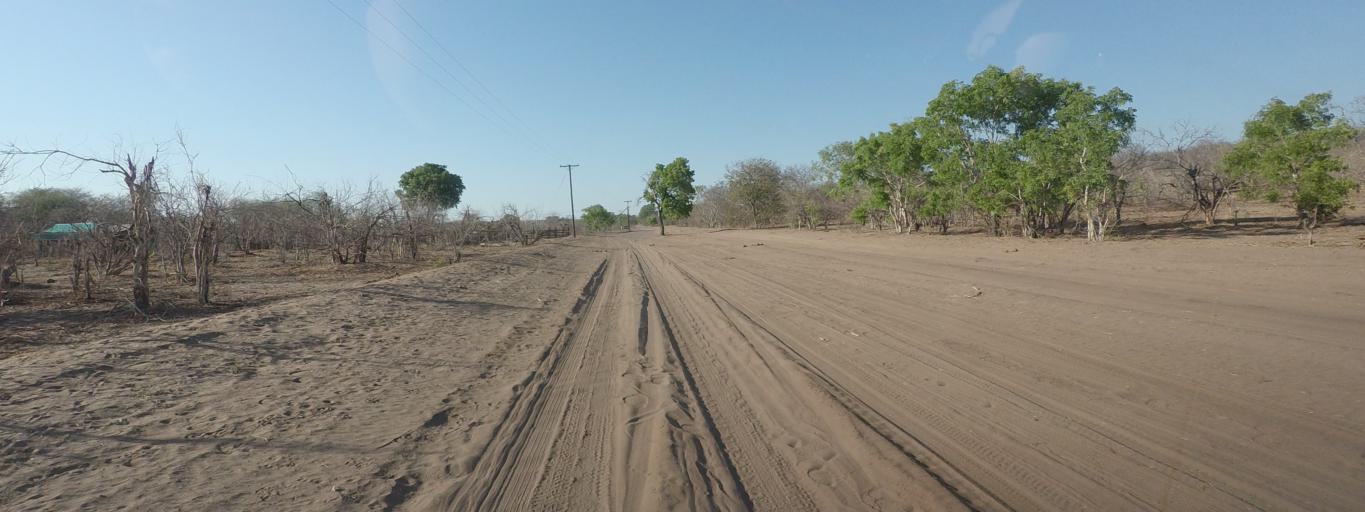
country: BW
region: North West
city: Kasane
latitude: -17.8879
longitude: 25.2297
